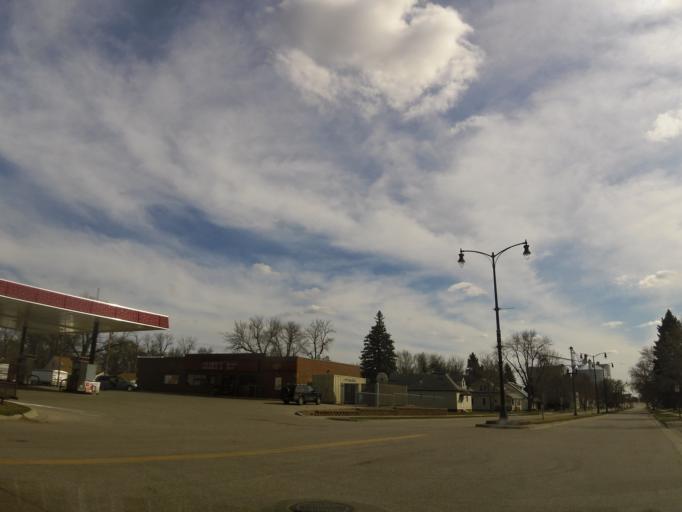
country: US
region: Minnesota
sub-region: Lac qui Parle County
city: Dawson
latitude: 44.9357
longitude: -96.0547
